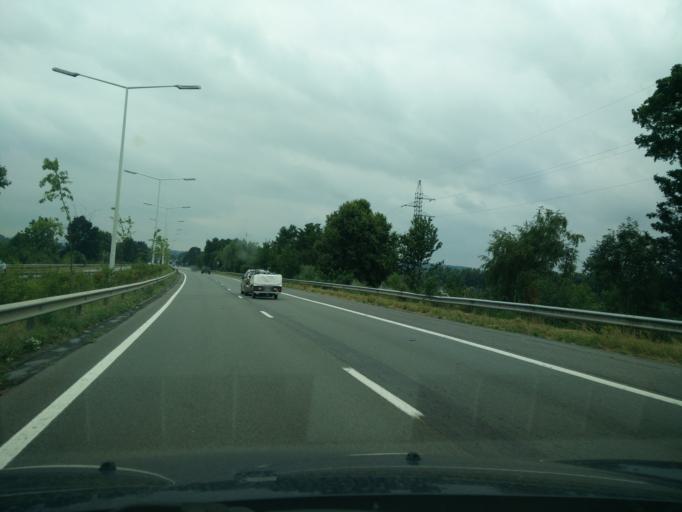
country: BE
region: Flanders
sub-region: Provincie Oost-Vlaanderen
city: Oudenaarde
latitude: 50.8497
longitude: 3.5917
